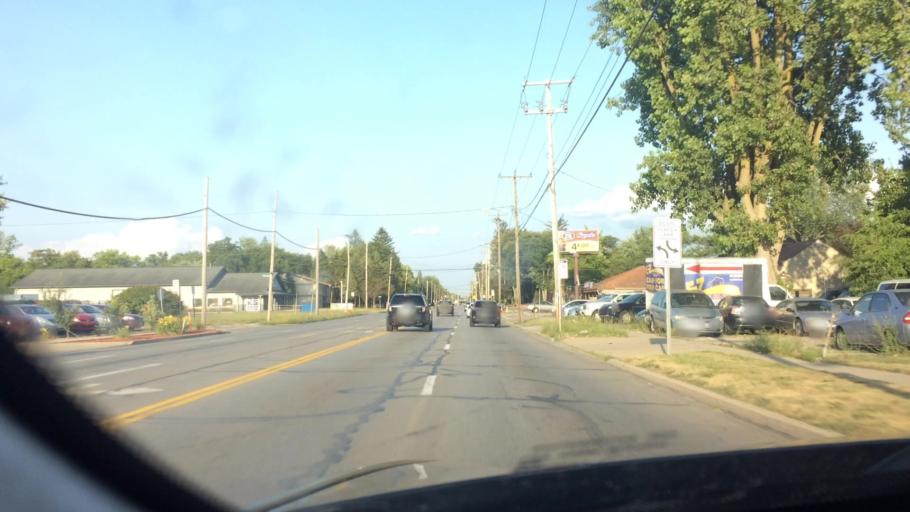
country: US
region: Ohio
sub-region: Lucas County
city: Ottawa Hills
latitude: 41.6537
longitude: -83.6821
